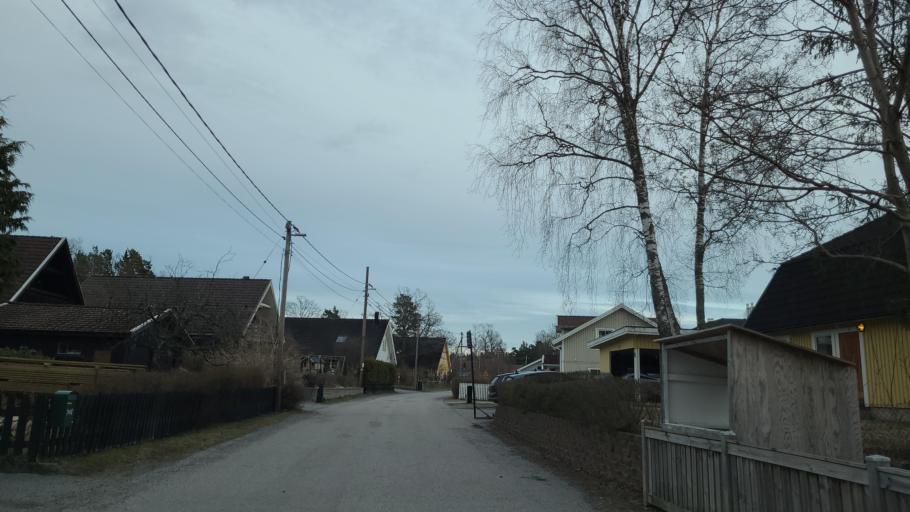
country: SE
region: Stockholm
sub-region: Nacka Kommun
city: Boo
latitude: 59.3200
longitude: 18.2637
